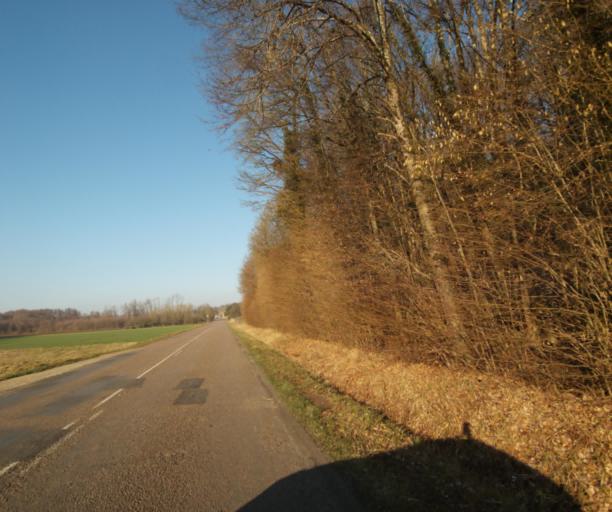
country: FR
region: Champagne-Ardenne
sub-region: Departement de la Haute-Marne
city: Chevillon
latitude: 48.5326
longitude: 5.1065
